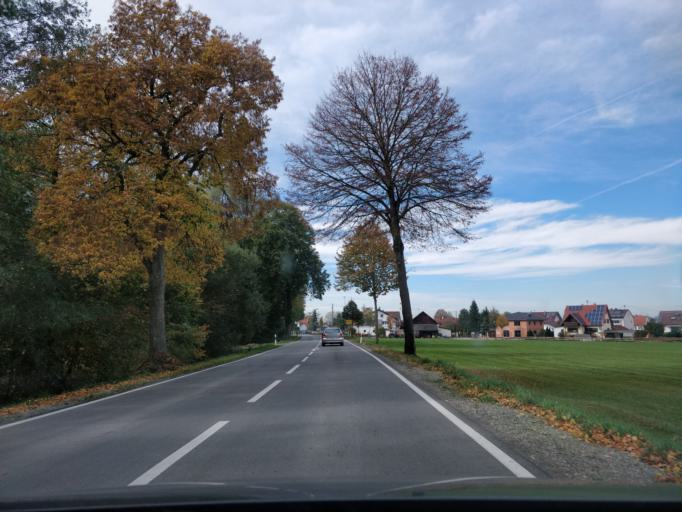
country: DE
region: Bavaria
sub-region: Swabia
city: Wiedergeltingen
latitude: 48.0368
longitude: 10.6817
